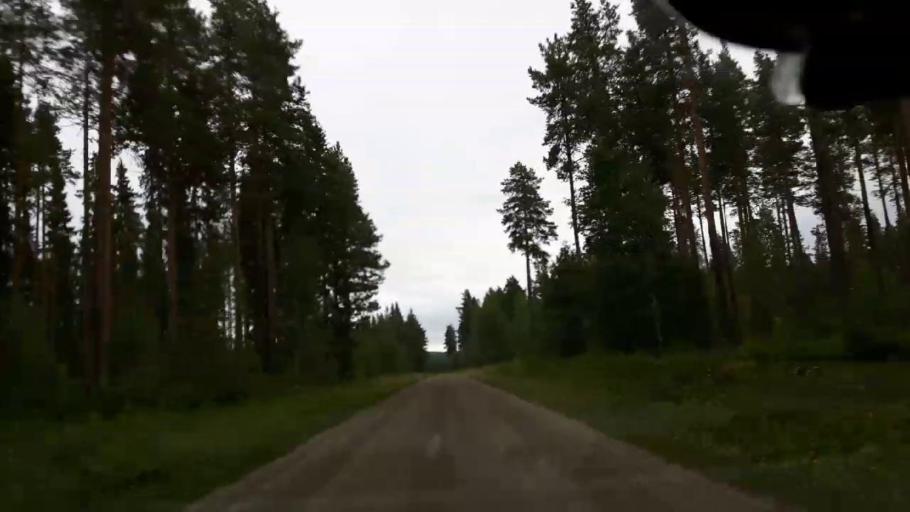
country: SE
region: Jaemtland
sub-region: Braecke Kommun
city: Braecke
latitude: 62.9424
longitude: 15.4502
